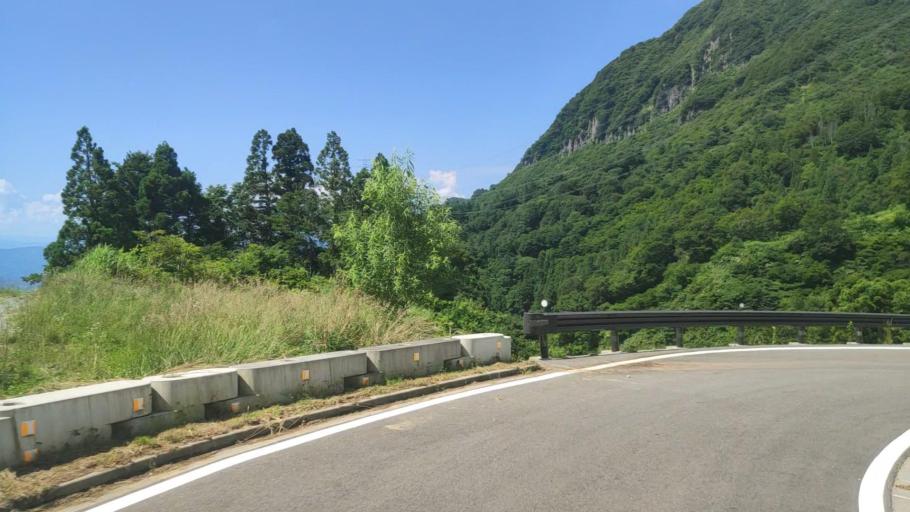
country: JP
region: Fukui
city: Katsuyama
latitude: 36.1477
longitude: 136.5231
